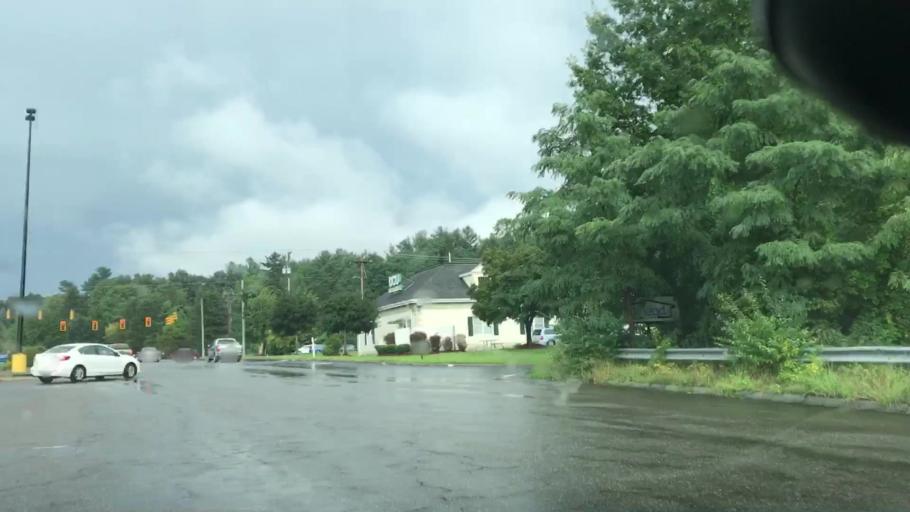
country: US
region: New Hampshire
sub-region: Hillsborough County
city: Hudson
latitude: 42.7256
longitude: -71.4253
